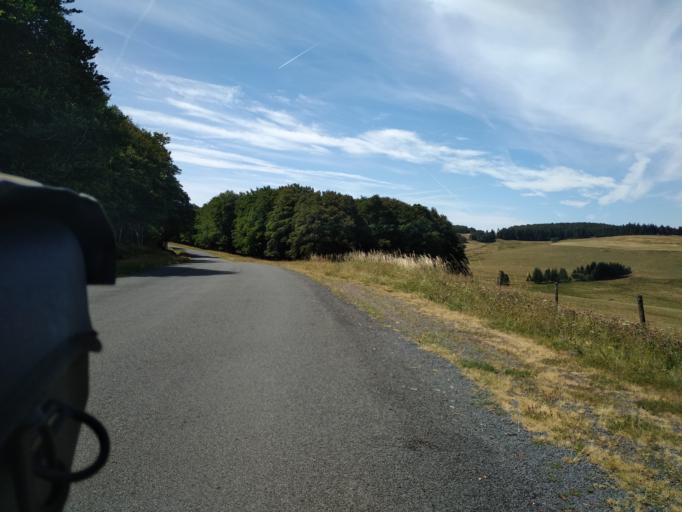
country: FR
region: Midi-Pyrenees
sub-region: Departement de l'Aveyron
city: Laguiole
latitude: 44.6645
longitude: 2.9591
